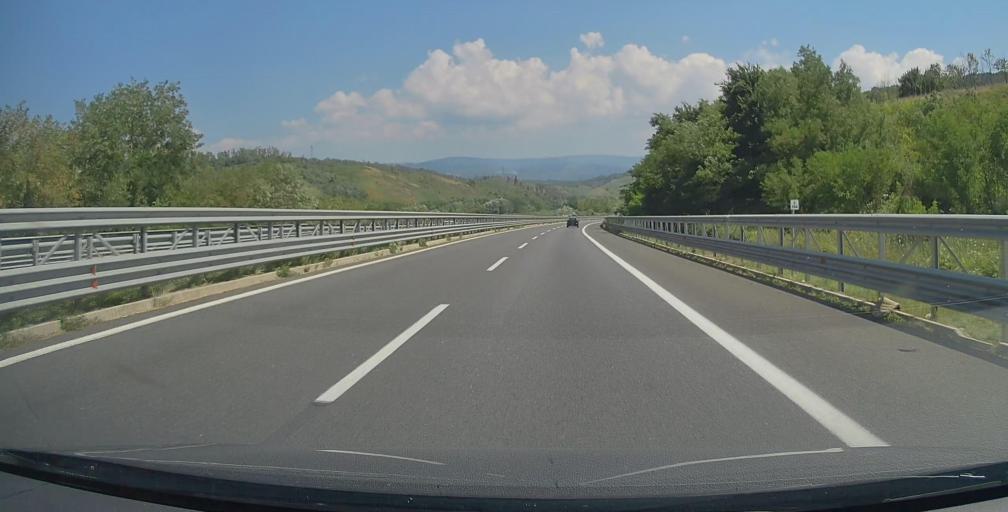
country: IT
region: Calabria
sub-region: Provincia di Vibo-Valentia
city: Maierato
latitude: 38.6691
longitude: 16.1835
